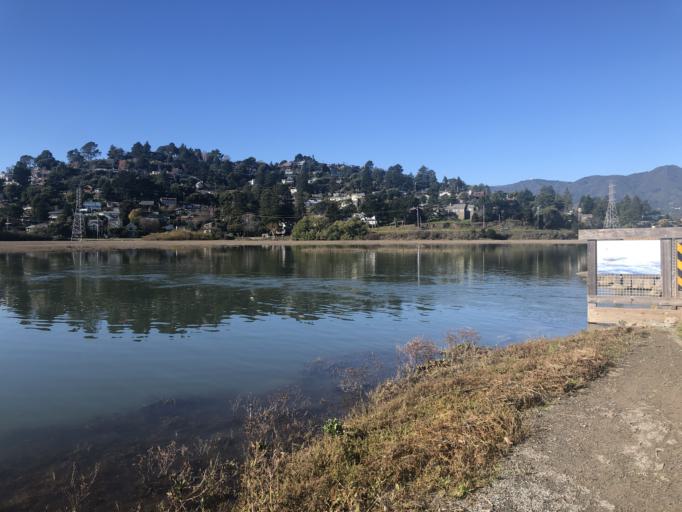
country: US
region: California
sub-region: Marin County
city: Tamalpais-Homestead Valley
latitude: 37.8840
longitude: -122.5207
